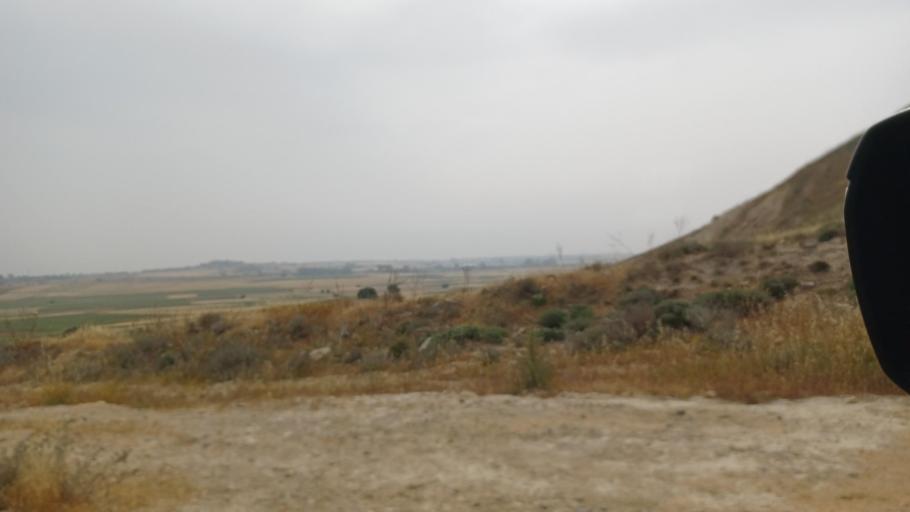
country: CY
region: Lefkosia
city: Mammari
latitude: 35.1661
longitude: 33.2321
